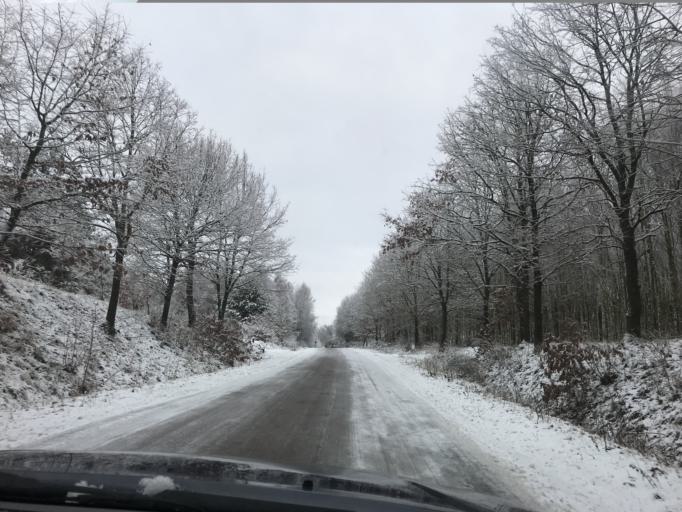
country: PL
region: Pomeranian Voivodeship
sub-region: Powiat bytowski
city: Parchowo
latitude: 54.2324
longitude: 17.5728
